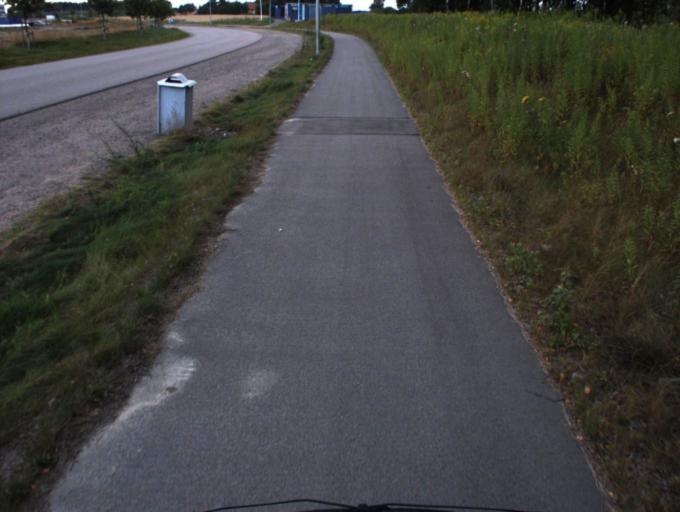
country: SE
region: Skane
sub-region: Helsingborg
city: Odakra
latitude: 56.0670
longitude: 12.7876
